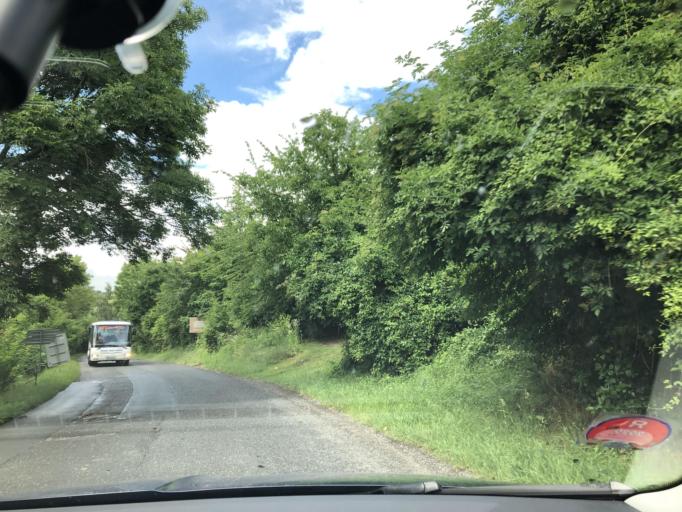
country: CZ
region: Central Bohemia
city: Nelahozeves
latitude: 50.2574
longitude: 14.2971
